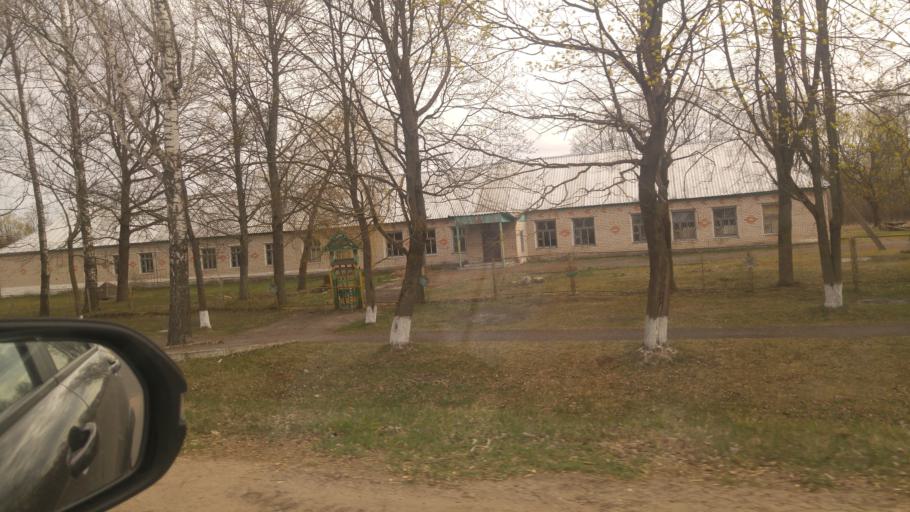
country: BY
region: Minsk
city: Chervyen'
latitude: 53.6473
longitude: 28.6251
